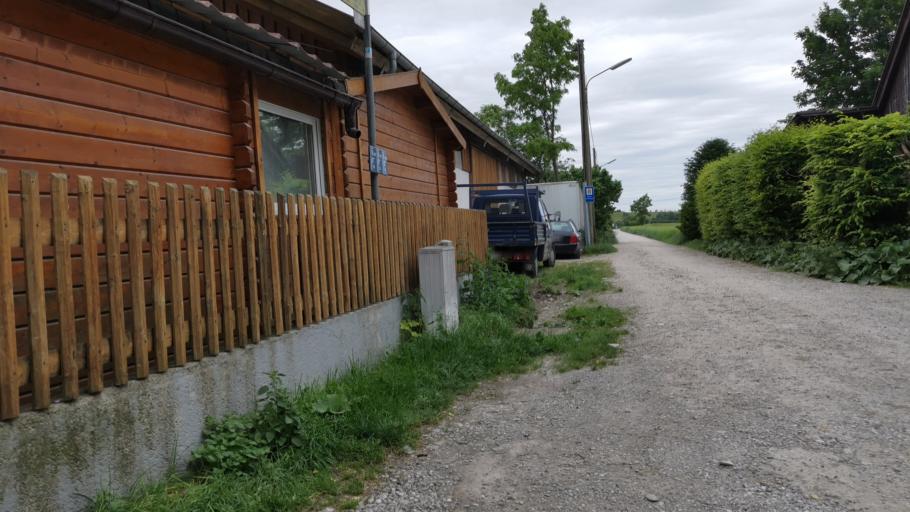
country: DE
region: Bavaria
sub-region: Upper Bavaria
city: Puchheim
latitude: 48.1353
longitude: 11.3522
